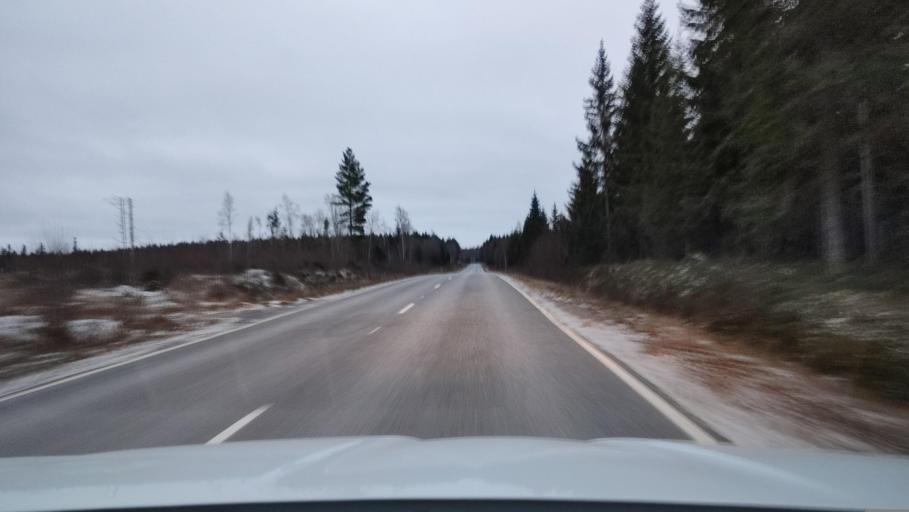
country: FI
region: Ostrobothnia
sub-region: Vaasa
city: Replot
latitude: 63.2444
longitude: 21.3810
